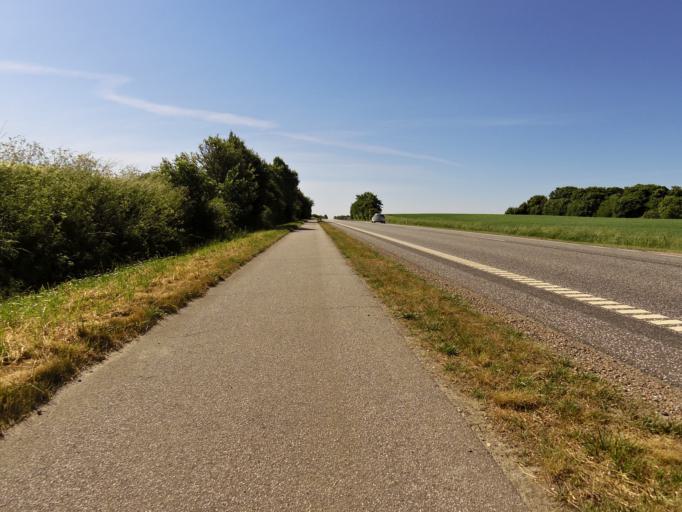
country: DK
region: Central Jutland
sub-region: Struer Kommune
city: Struer
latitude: 56.4562
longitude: 8.5914
